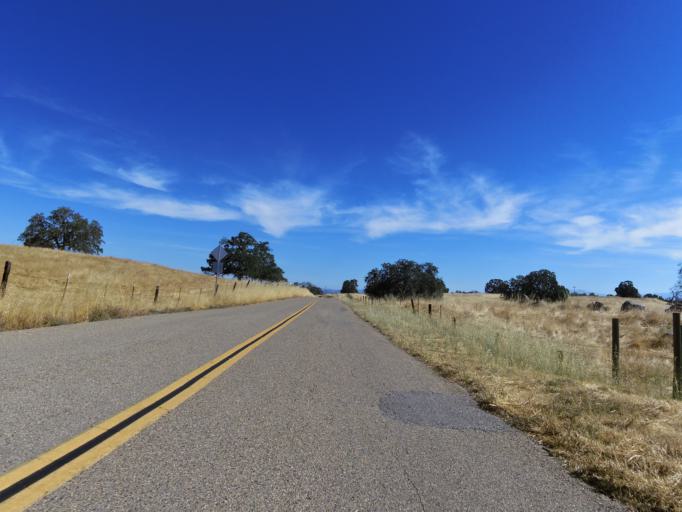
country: US
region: California
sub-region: Madera County
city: Yosemite Lakes
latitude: 37.2357
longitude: -119.9205
